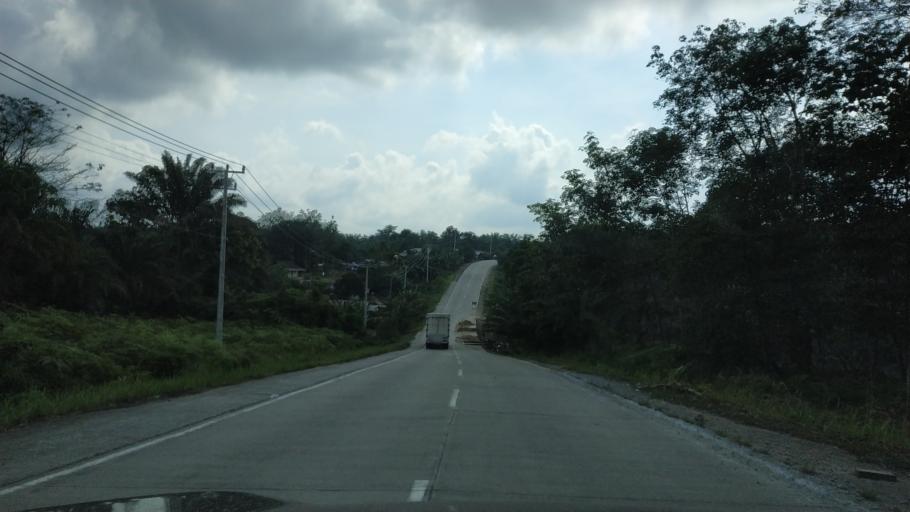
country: ID
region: Riau
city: Pangkalan Kasai
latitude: -0.6965
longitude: 102.4861
